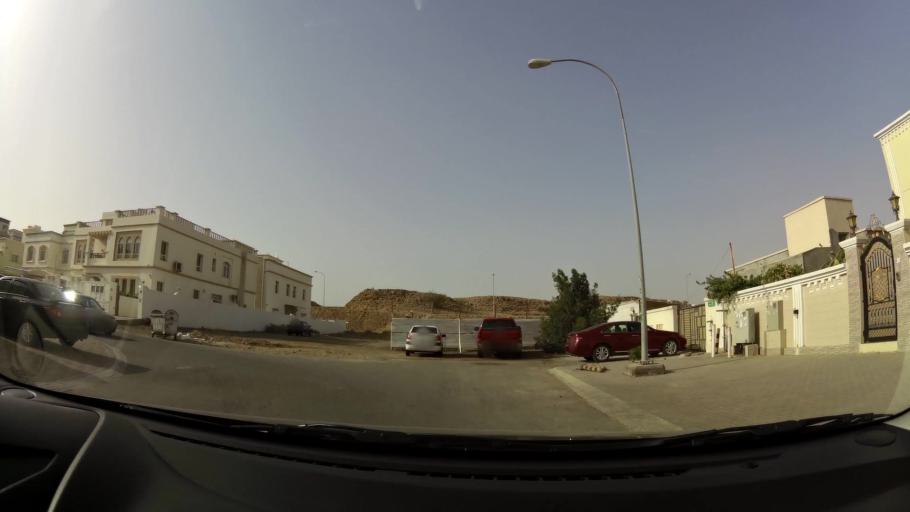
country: OM
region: Muhafazat Masqat
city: Bawshar
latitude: 23.5518
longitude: 58.3638
